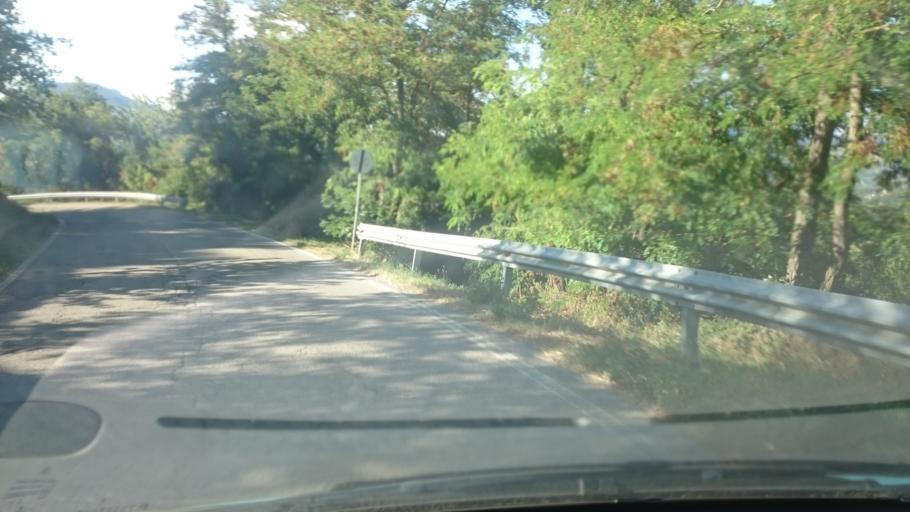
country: IT
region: Emilia-Romagna
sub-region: Provincia di Reggio Emilia
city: Villa Minozzo
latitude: 44.3701
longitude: 10.4644
